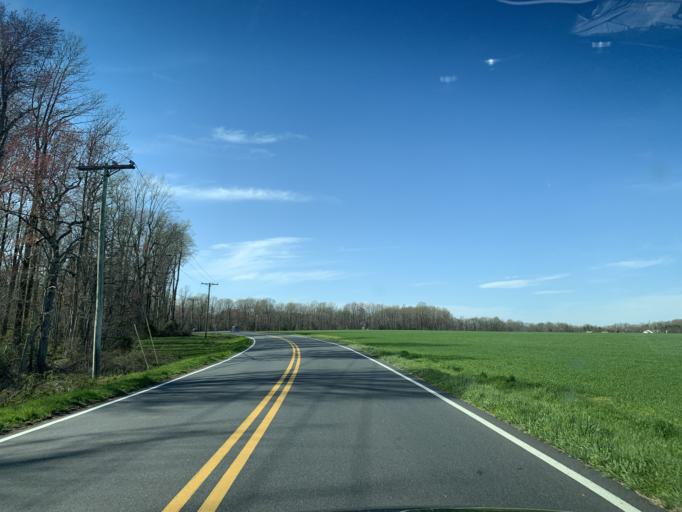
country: US
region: Delaware
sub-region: Kent County
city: Riverview
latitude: 38.9626
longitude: -75.4820
